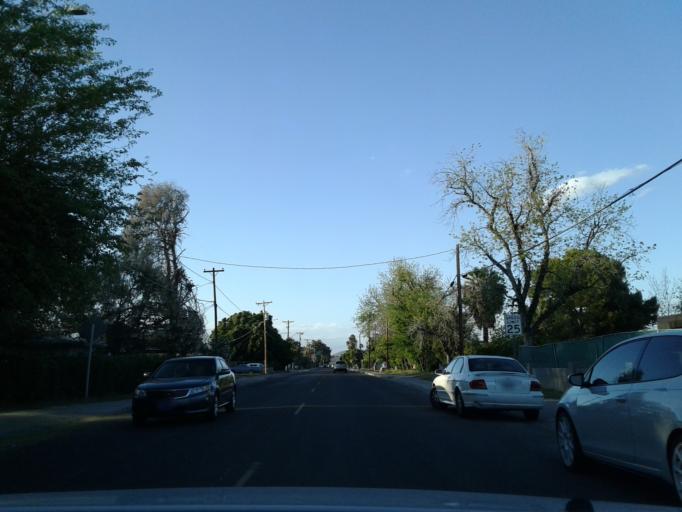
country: US
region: Arizona
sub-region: Maricopa County
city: Phoenix
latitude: 33.5138
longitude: -112.0956
